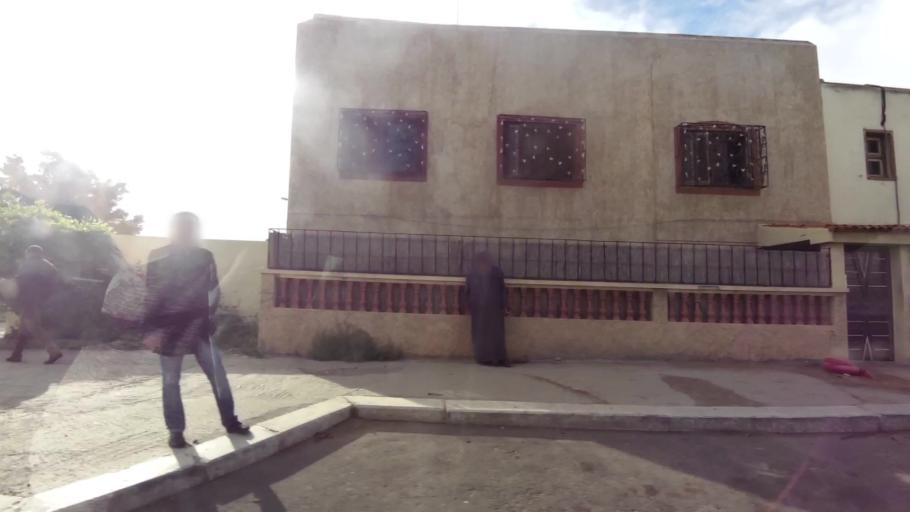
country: MA
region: Doukkala-Abda
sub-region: El-Jadida
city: El Jadida
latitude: 33.2472
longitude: -8.5184
